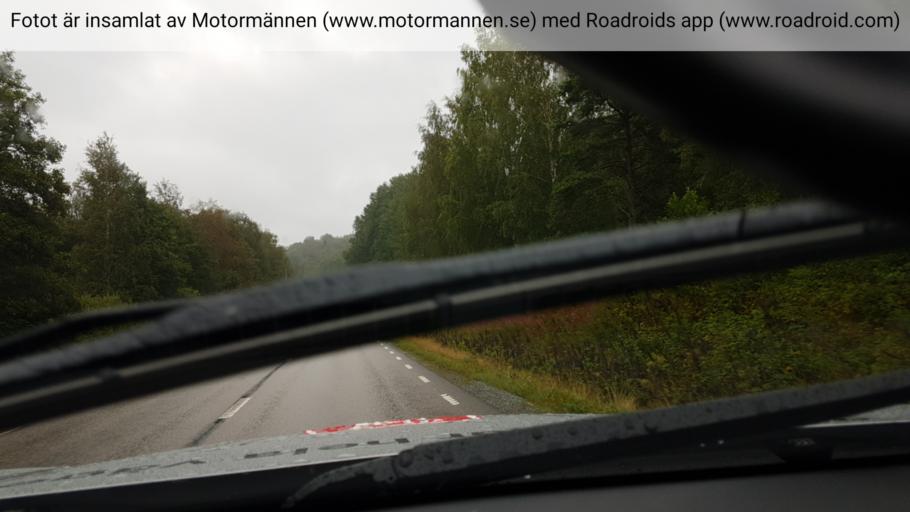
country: SE
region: Vaestra Goetaland
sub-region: Bengtsfors Kommun
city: Dals Langed
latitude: 58.8736
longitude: 12.2075
